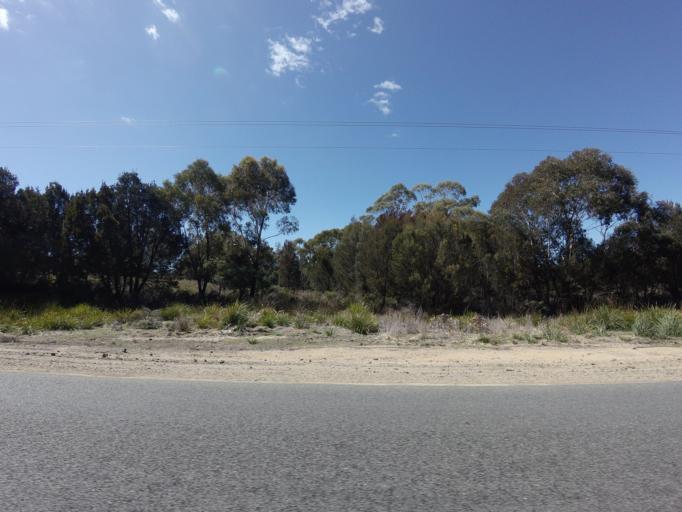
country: AU
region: Tasmania
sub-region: Break O'Day
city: St Helens
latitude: -41.6785
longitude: 148.2787
